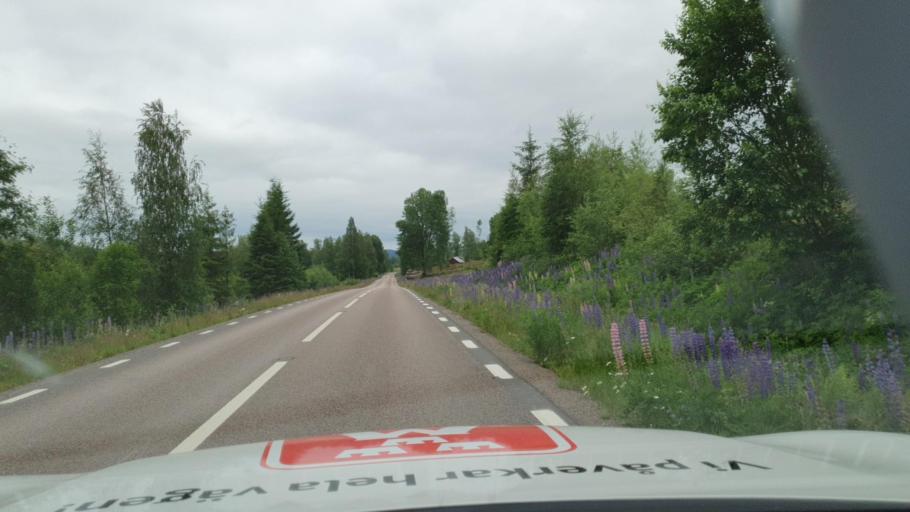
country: SE
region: Vaermland
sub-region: Sunne Kommun
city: Sunne
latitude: 59.9022
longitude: 12.9092
